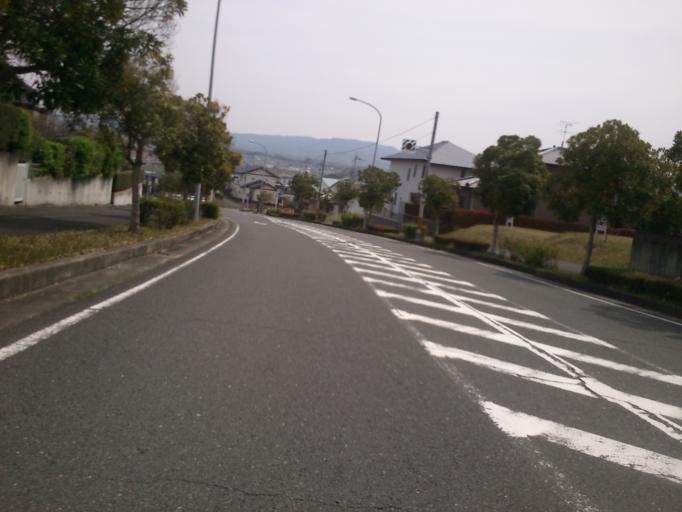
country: JP
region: Nara
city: Nara-shi
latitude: 34.7253
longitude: 135.7978
